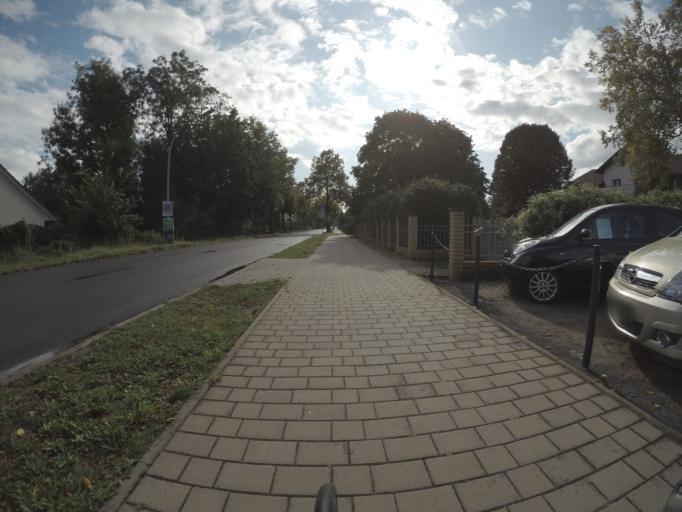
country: DE
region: Brandenburg
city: Rehfelde
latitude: 52.5345
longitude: 13.8462
